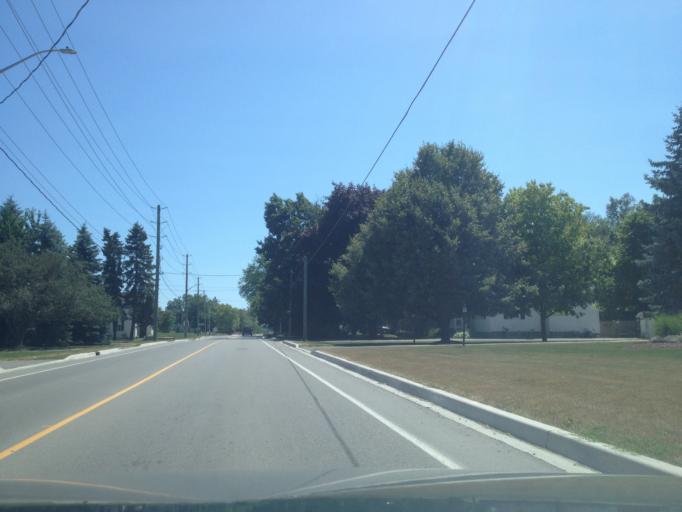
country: CA
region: Ontario
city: Waterloo
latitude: 43.5405
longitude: -80.5104
